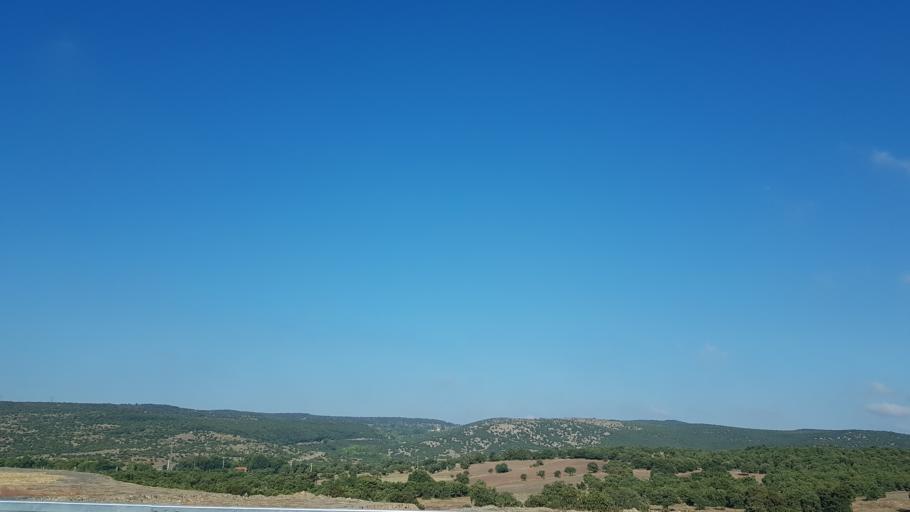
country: TR
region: Balikesir
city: Ertugrul
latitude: 39.5166
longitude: 27.6819
